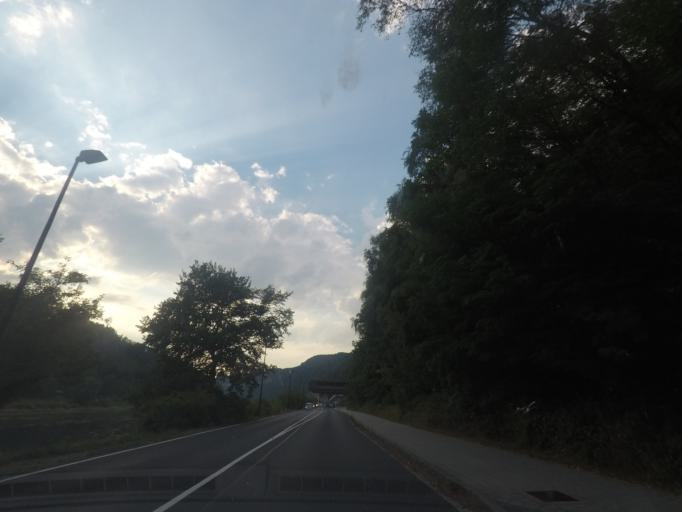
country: DE
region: Saxony
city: Bad Schandau
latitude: 50.8883
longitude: 14.2338
